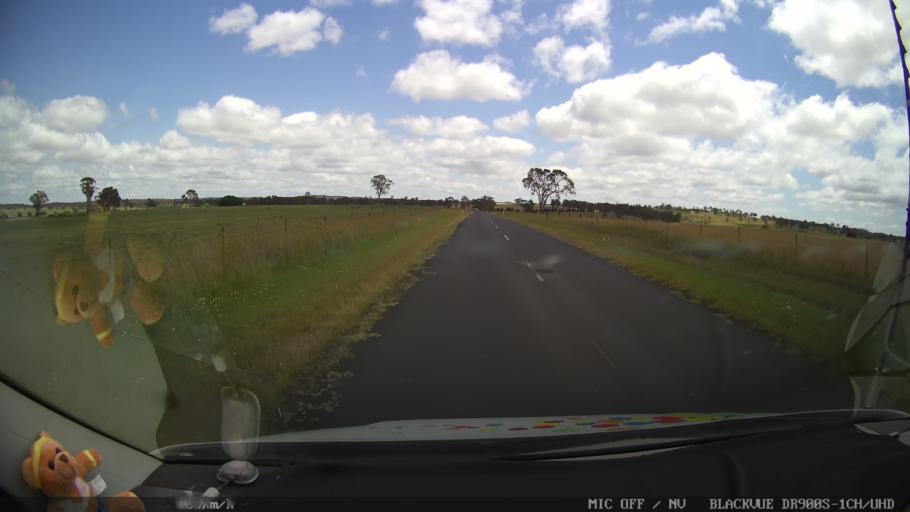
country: AU
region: New South Wales
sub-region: Glen Innes Severn
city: Glen Innes
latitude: -29.6581
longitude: 151.6927
